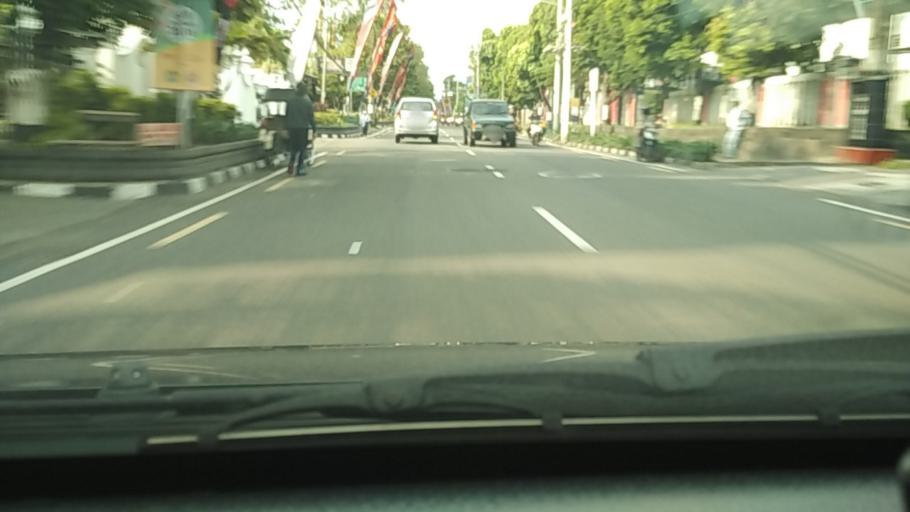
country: ID
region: Daerah Istimewa Yogyakarta
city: Yogyakarta
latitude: -7.7989
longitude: 110.3847
